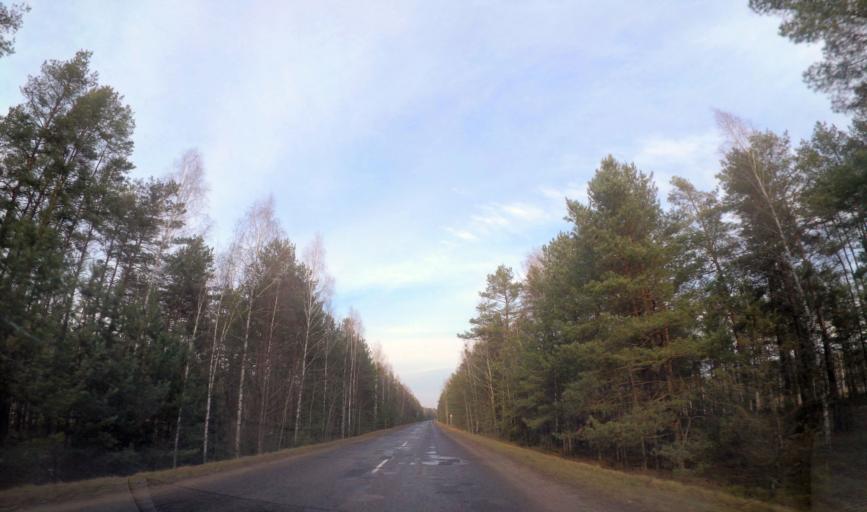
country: BY
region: Grodnenskaya
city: Hrodna
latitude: 53.7949
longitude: 24.0083
